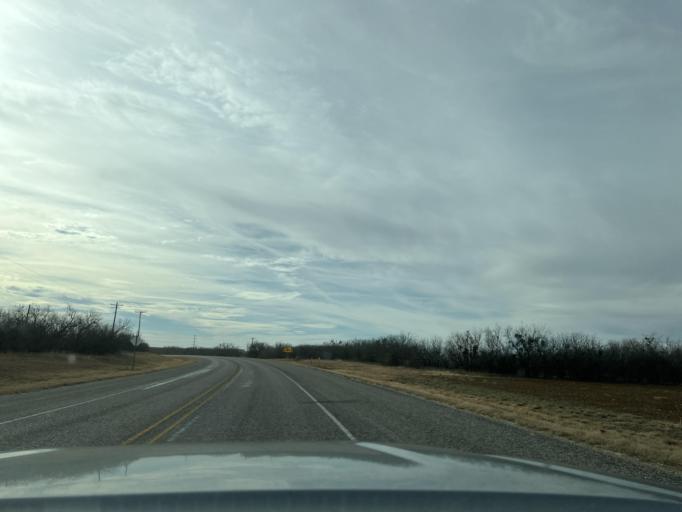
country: US
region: Texas
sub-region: Jones County
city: Stamford
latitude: 32.7654
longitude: -99.5949
